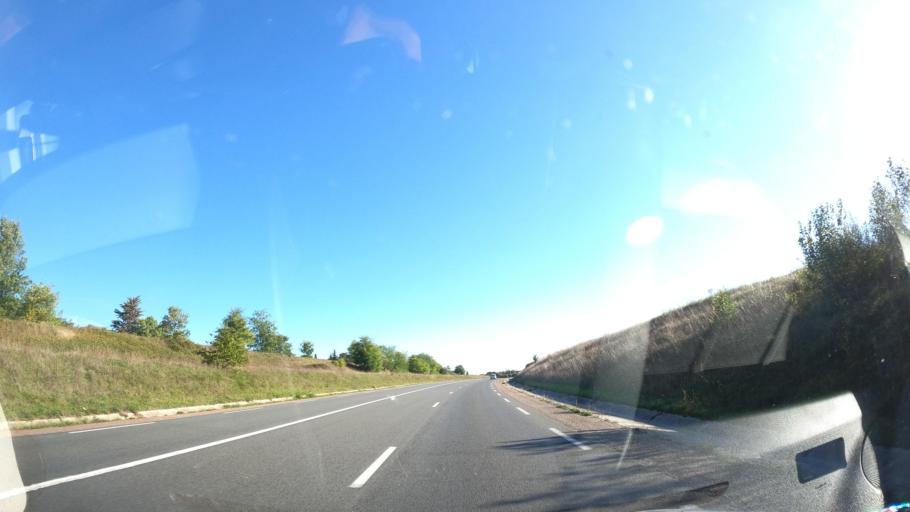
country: FR
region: Aquitaine
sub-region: Departement de la Dordogne
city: Creysse
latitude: 44.8609
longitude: 0.5422
